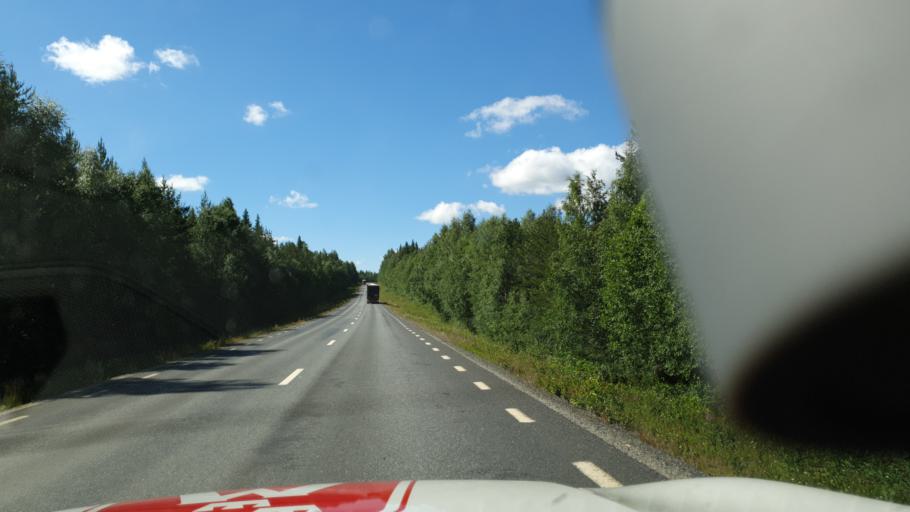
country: SE
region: Vaesterbotten
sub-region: Lycksele Kommun
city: Lycksele
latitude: 64.7641
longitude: 18.7108
